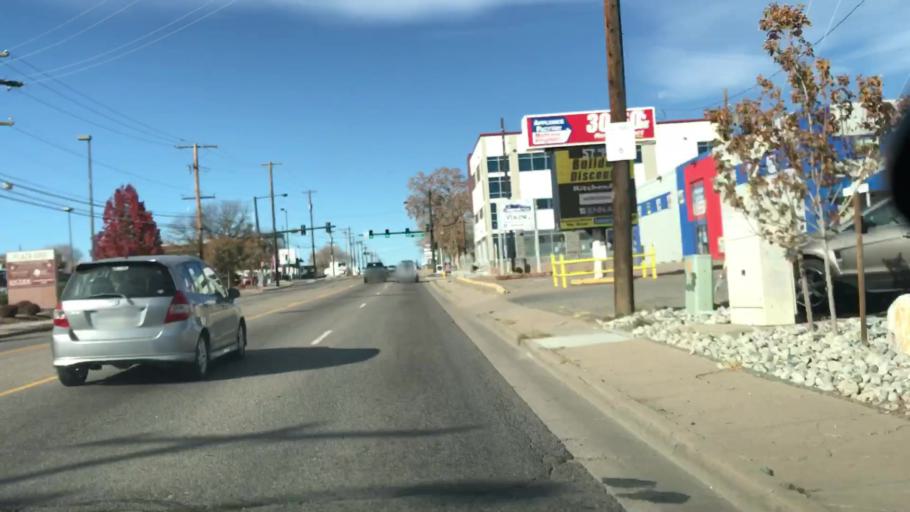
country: US
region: Colorado
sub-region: Arapahoe County
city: Glendale
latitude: 39.6785
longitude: -104.9175
